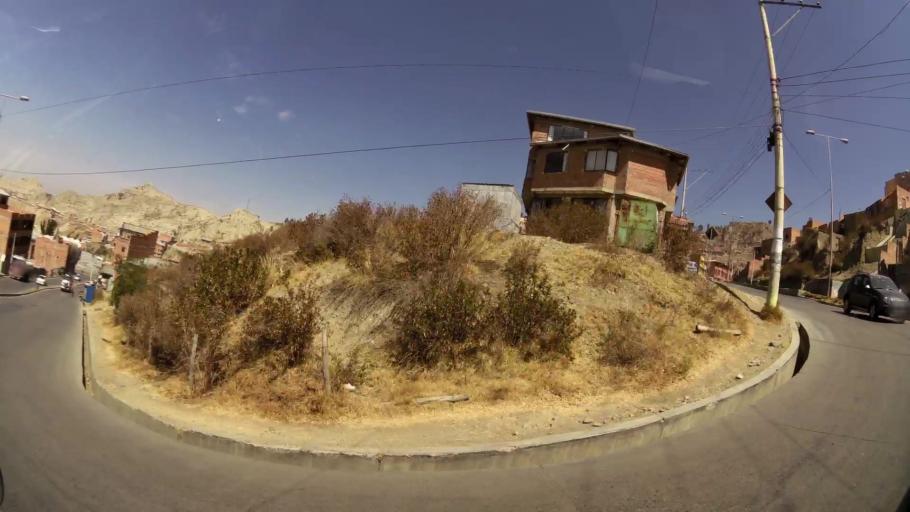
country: BO
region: La Paz
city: La Paz
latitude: -16.5324
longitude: -68.1422
